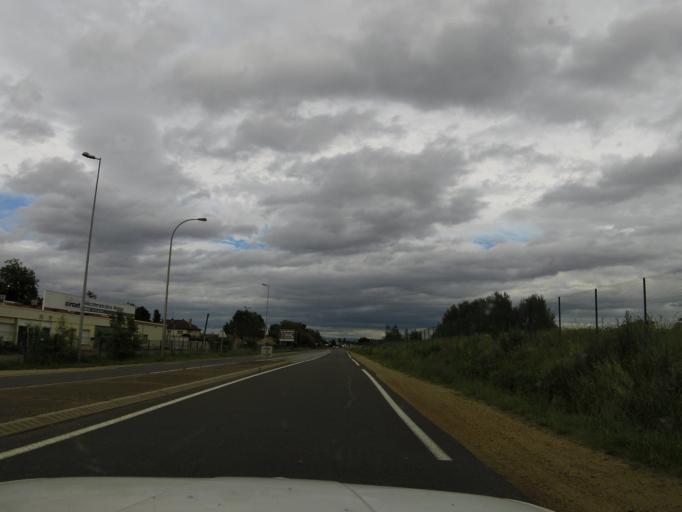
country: FR
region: Auvergne
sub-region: Departement du Puy-de-Dome
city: Gerzat
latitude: 45.8137
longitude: 3.1380
